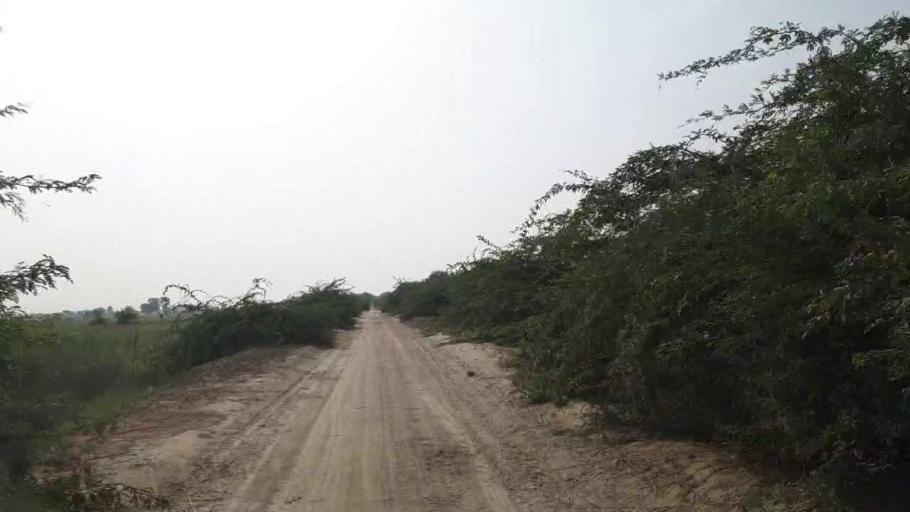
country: PK
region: Sindh
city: Kario
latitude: 24.7848
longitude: 68.5637
